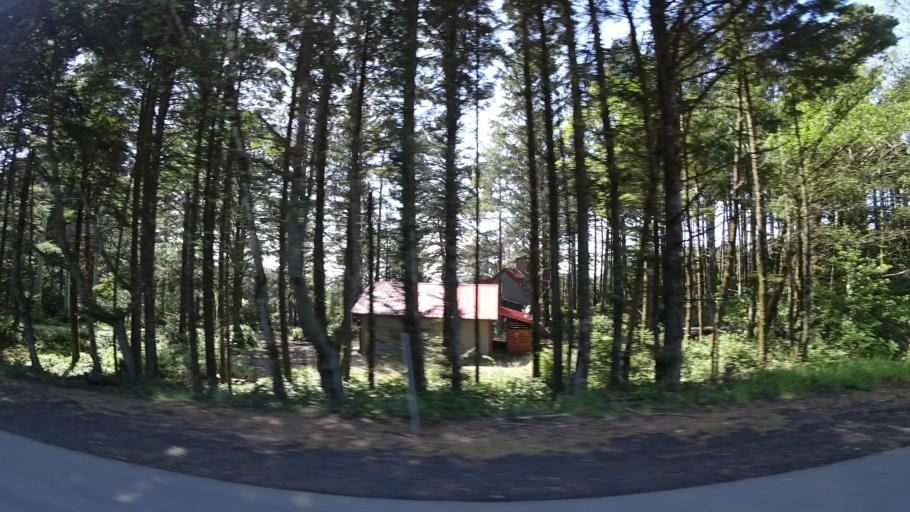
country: US
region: Oregon
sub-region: Lincoln County
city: Newport
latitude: 44.6873
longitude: -124.0637
